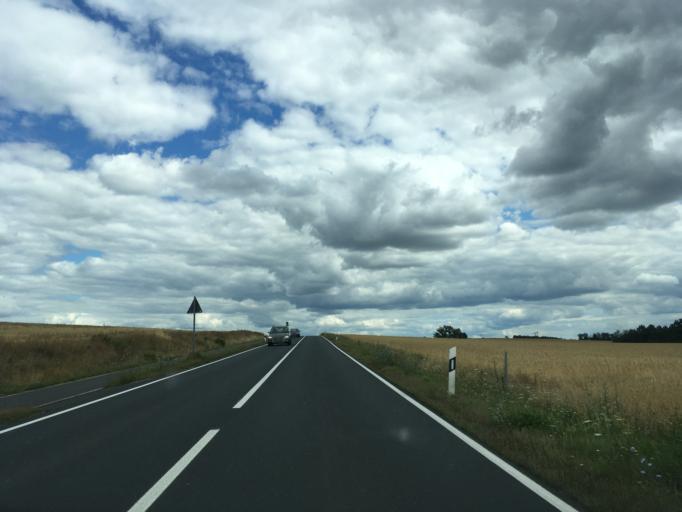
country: DE
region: Saxony
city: Ottendorf-Okrilla
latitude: 51.1667
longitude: 13.8642
